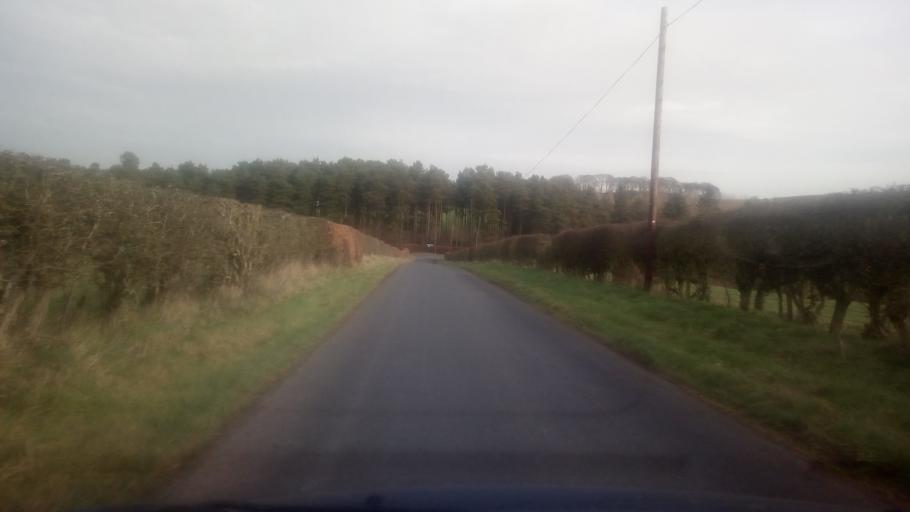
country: GB
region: Scotland
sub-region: The Scottish Borders
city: Hawick
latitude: 55.4367
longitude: -2.6934
